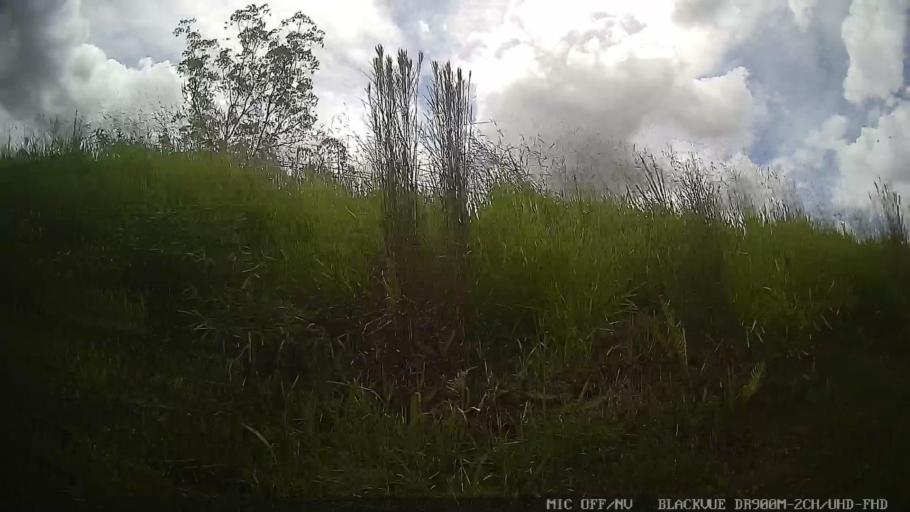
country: BR
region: Sao Paulo
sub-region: Suzano
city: Suzano
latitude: -23.6134
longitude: -46.3142
